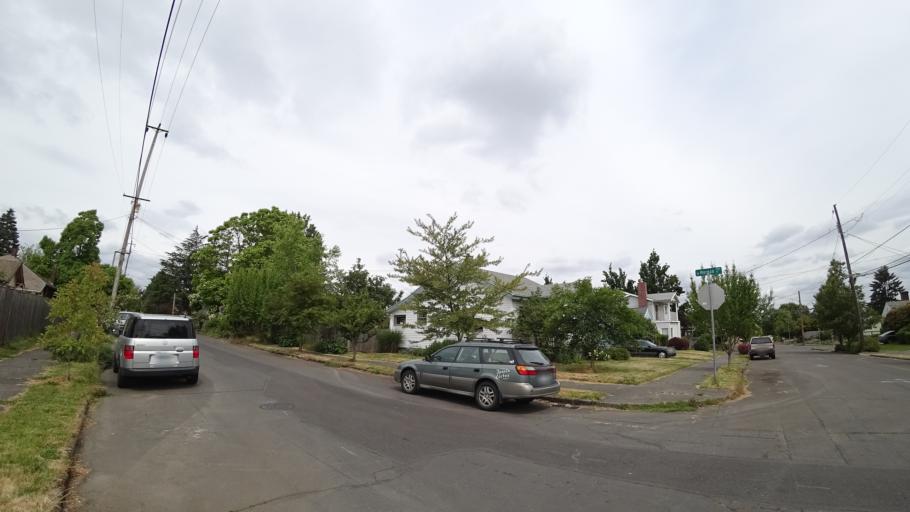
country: US
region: Oregon
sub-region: Multnomah County
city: Portland
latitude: 45.5744
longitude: -122.6708
